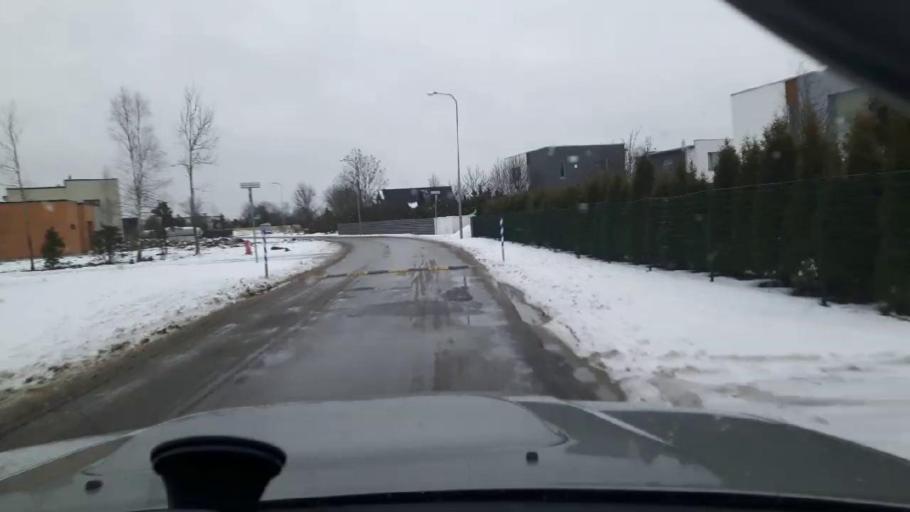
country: EE
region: Harju
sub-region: Harku vald
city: Tabasalu
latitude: 59.4578
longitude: 24.4502
